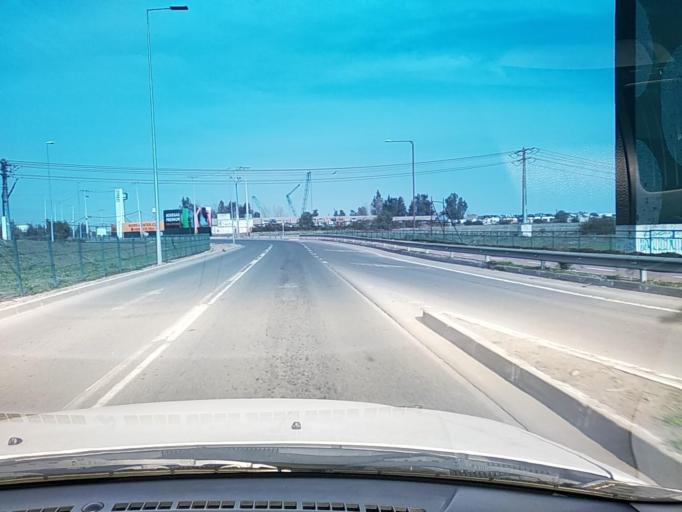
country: CL
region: Santiago Metropolitan
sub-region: Provincia de Chacabuco
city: Chicureo Abajo
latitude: -33.3016
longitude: -70.7308
